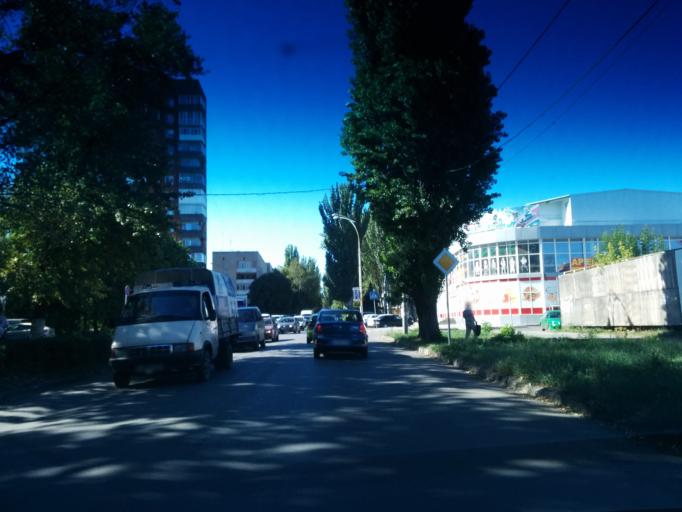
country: RU
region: Rostov
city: Shakhty
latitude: 47.7108
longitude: 40.2165
